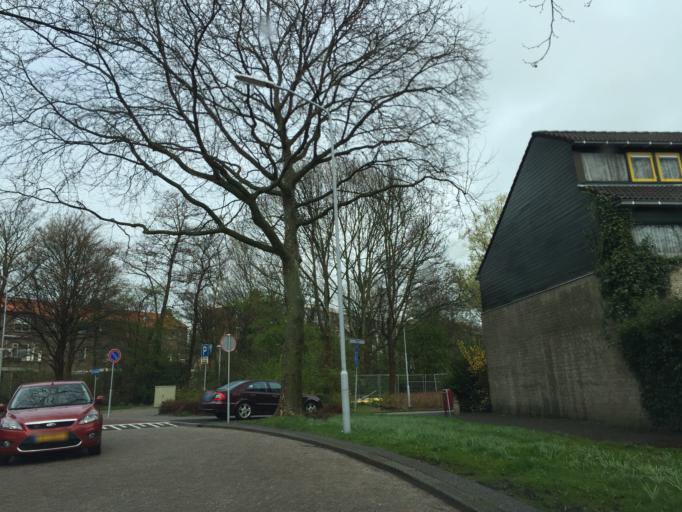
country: NL
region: South Holland
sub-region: Gemeente Leidschendam-Voorburg
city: Voorburg
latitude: 52.0778
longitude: 4.4005
